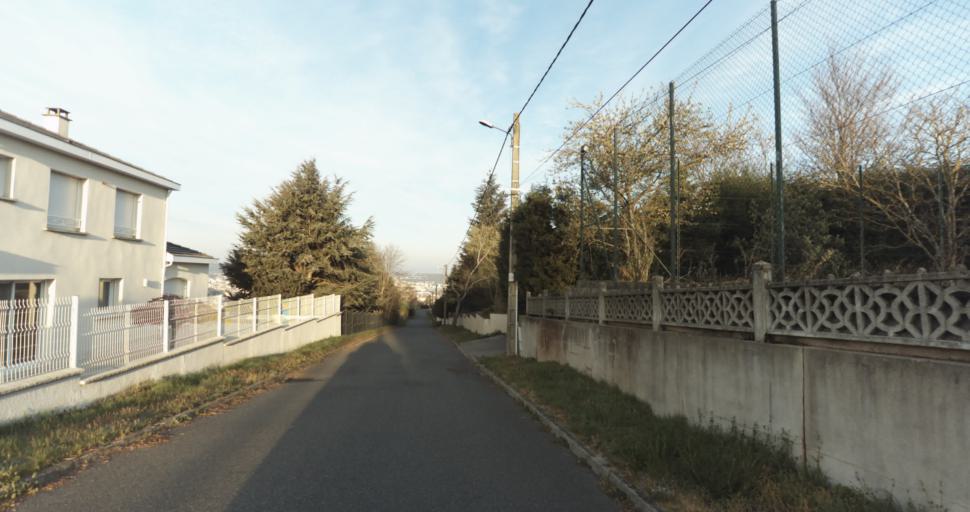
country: FR
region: Rhone-Alpes
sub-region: Departement de la Loire
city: Saint-Jean-Bonnefonds
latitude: 45.4498
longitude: 4.4373
